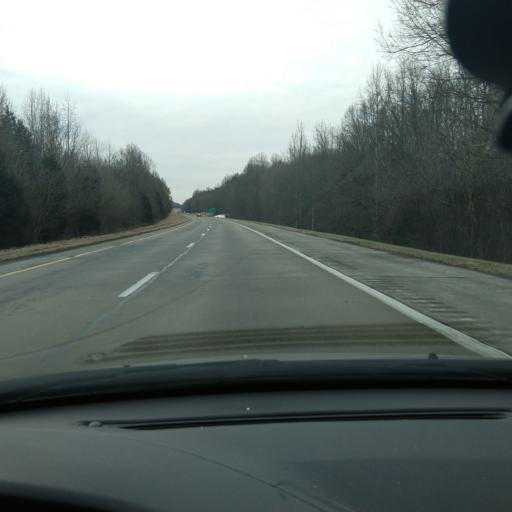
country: US
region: North Carolina
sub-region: Davidson County
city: Midway
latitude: 35.9904
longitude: -80.2381
